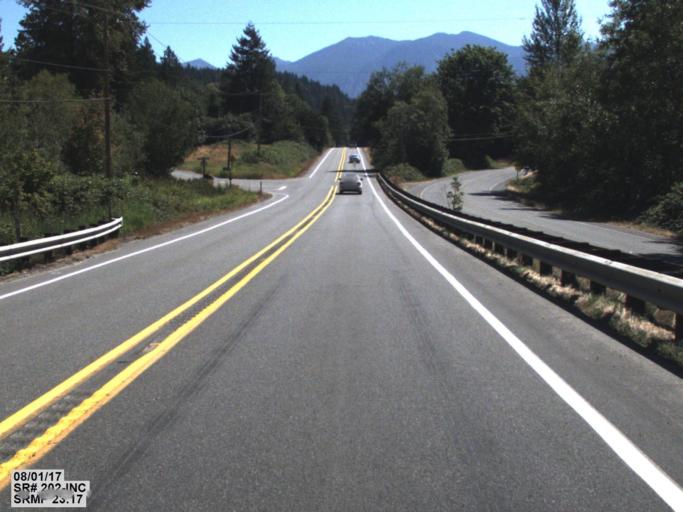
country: US
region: Washington
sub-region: King County
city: Fall City
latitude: 47.5617
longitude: -121.8626
